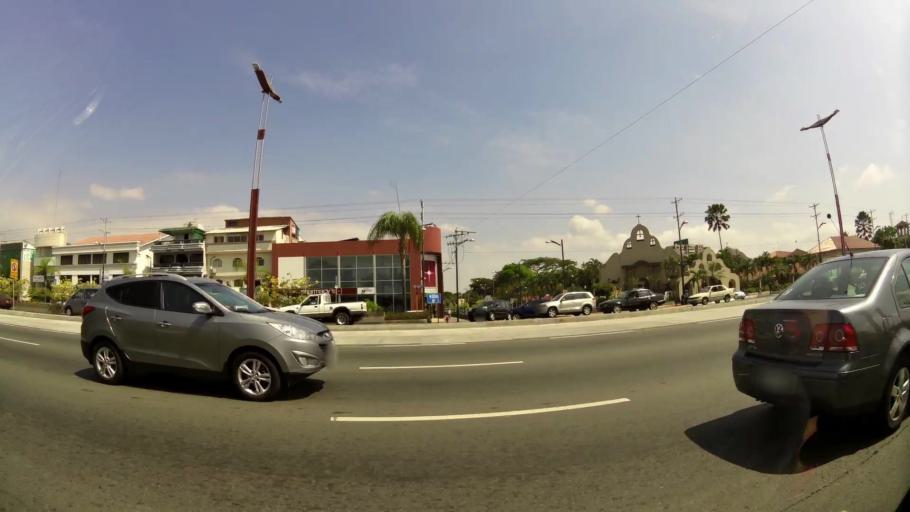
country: EC
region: Guayas
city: Eloy Alfaro
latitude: -2.1460
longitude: -79.8638
